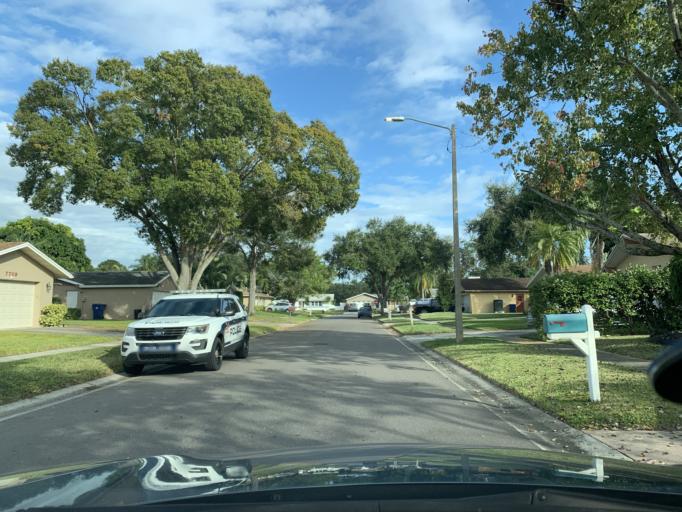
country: US
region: Florida
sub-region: Pinellas County
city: Kenneth City
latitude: 27.8222
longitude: -82.7449
